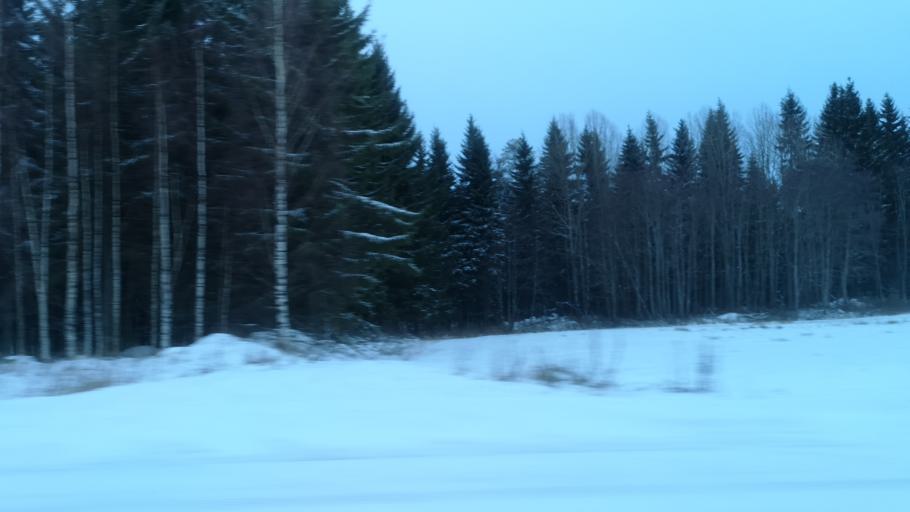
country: FI
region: Southern Savonia
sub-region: Savonlinna
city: Enonkoski
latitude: 62.0726
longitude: 28.7234
